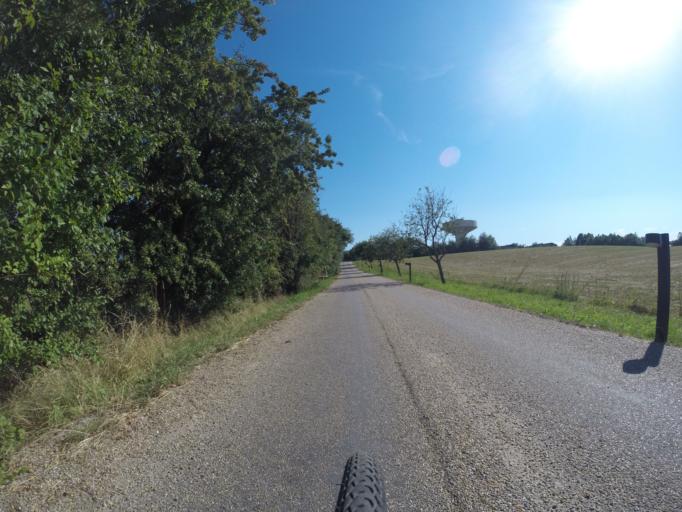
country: DK
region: Capital Region
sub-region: Herlev Kommune
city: Herlev
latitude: 55.7465
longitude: 12.4324
